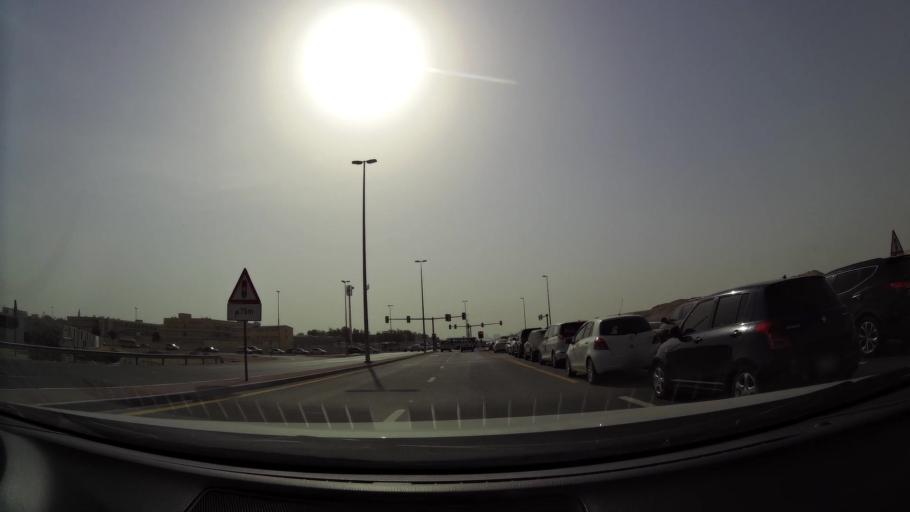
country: AE
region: Ash Shariqah
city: Sharjah
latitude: 25.2713
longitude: 55.4404
